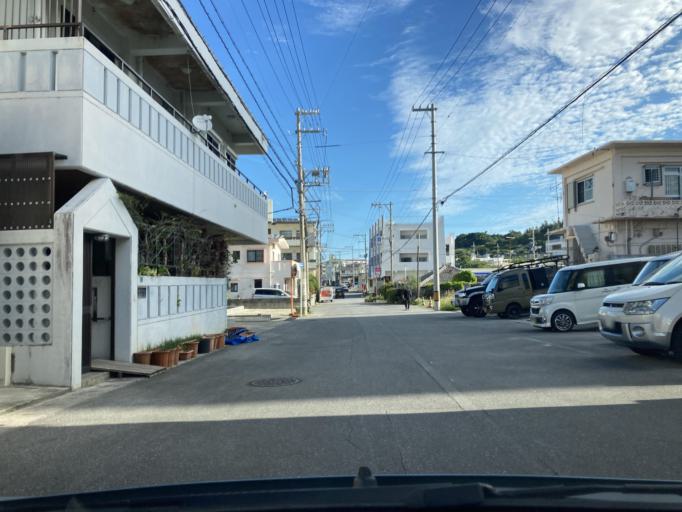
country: JP
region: Okinawa
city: Ginowan
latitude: 26.2674
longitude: 127.7365
